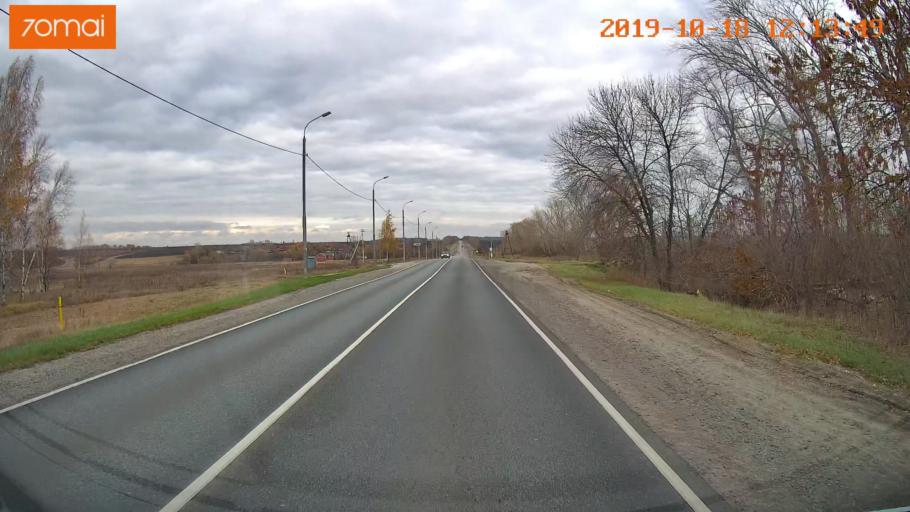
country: RU
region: Rjazan
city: Zakharovo
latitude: 54.4238
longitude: 39.3739
